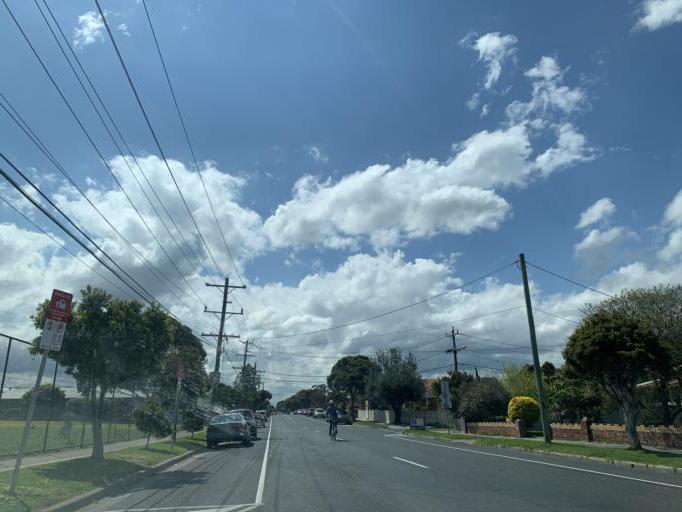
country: AU
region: Victoria
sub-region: Kingston
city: Mordialloc
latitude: -38.0077
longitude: 145.0924
